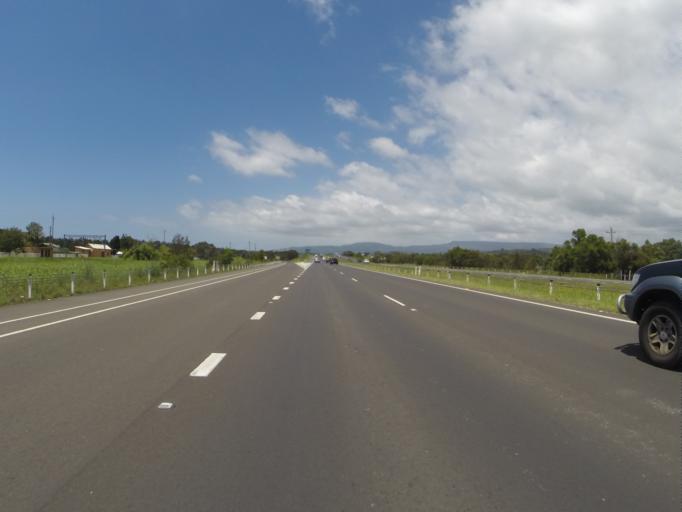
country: AU
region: New South Wales
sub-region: Shellharbour
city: Croom
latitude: -34.6044
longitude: 150.8398
